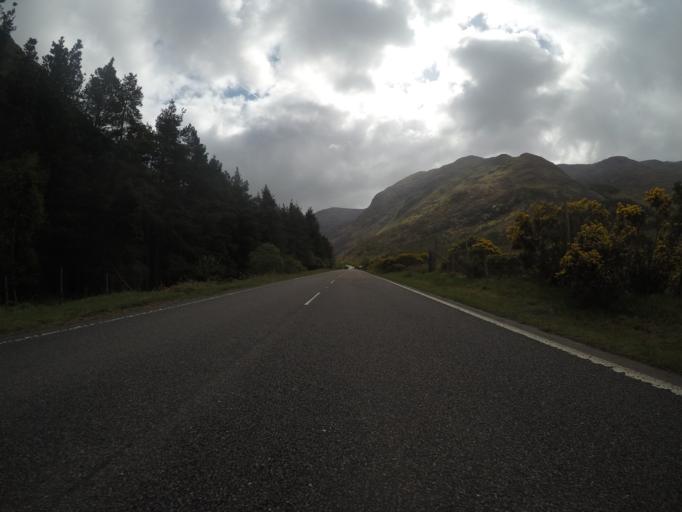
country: GB
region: Scotland
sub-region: Highland
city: Fort William
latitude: 57.1708
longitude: -5.3559
